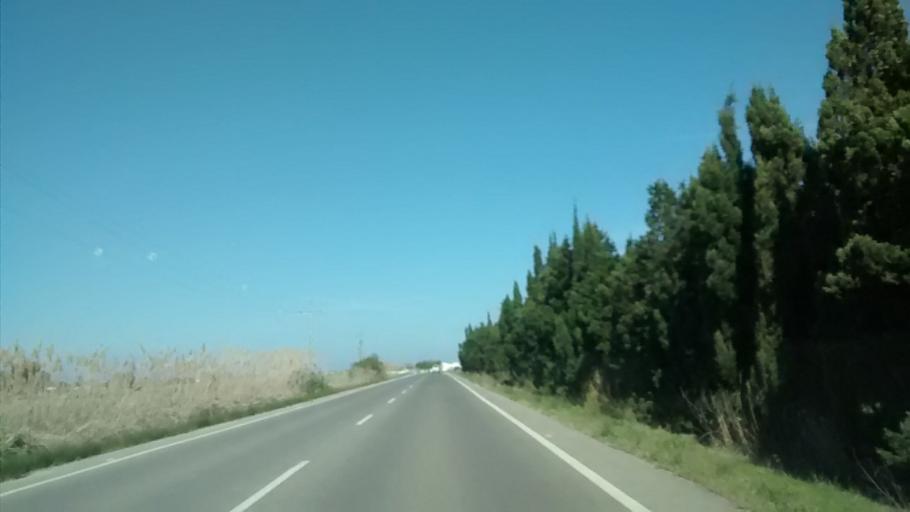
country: ES
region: Catalonia
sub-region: Provincia de Tarragona
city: Deltebre
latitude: 40.7104
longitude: 0.8165
